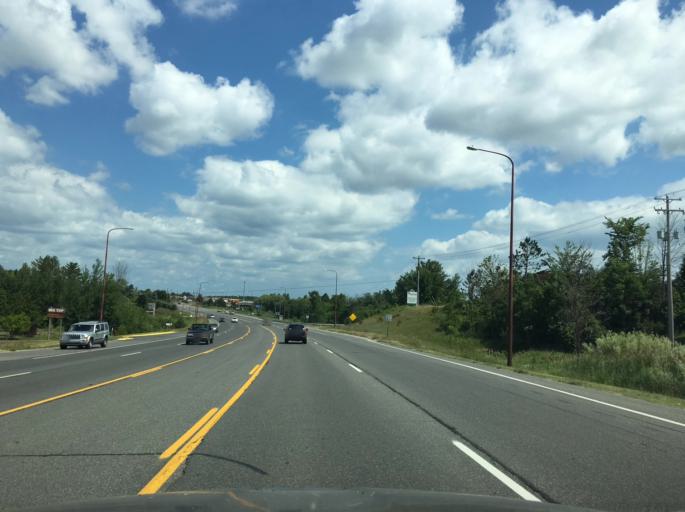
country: US
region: Michigan
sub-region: Grand Traverse County
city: Traverse City
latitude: 44.7165
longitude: -85.6470
